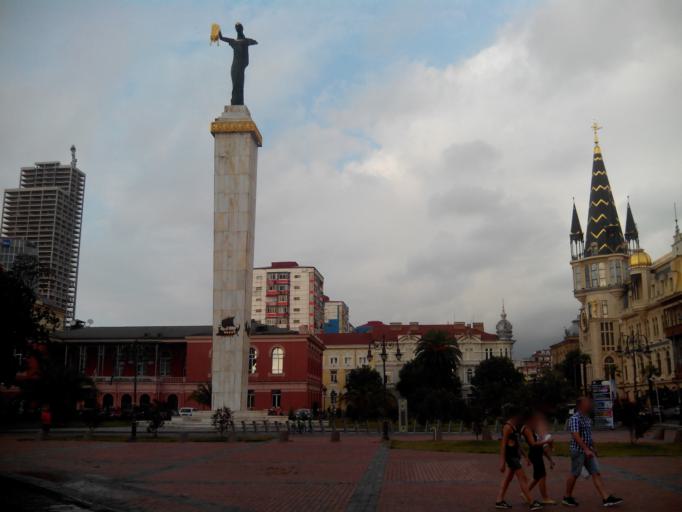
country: GE
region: Ajaria
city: Batumi
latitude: 41.6511
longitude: 41.6358
